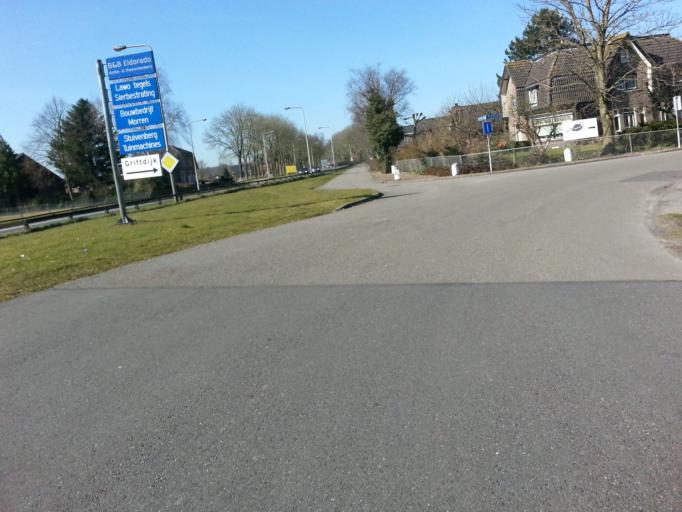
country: NL
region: Utrecht
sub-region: Gemeente Woudenberg
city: Woudenberg
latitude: 52.0821
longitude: 5.4037
